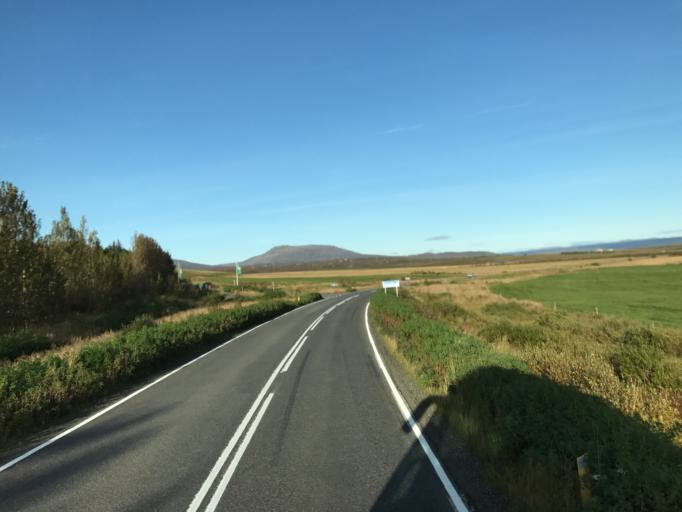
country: IS
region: South
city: Selfoss
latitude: 64.2384
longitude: -20.5520
